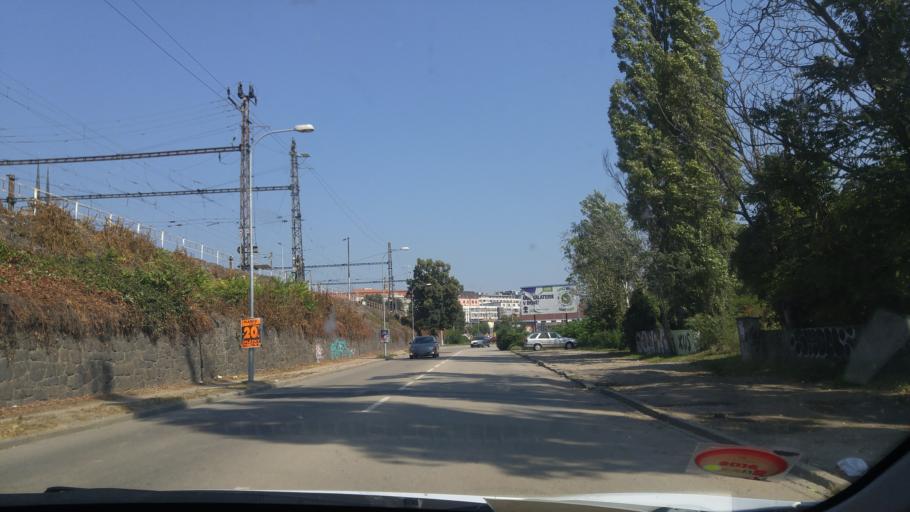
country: CZ
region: South Moravian
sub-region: Mesto Brno
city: Brno
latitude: 49.1867
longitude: 16.6091
